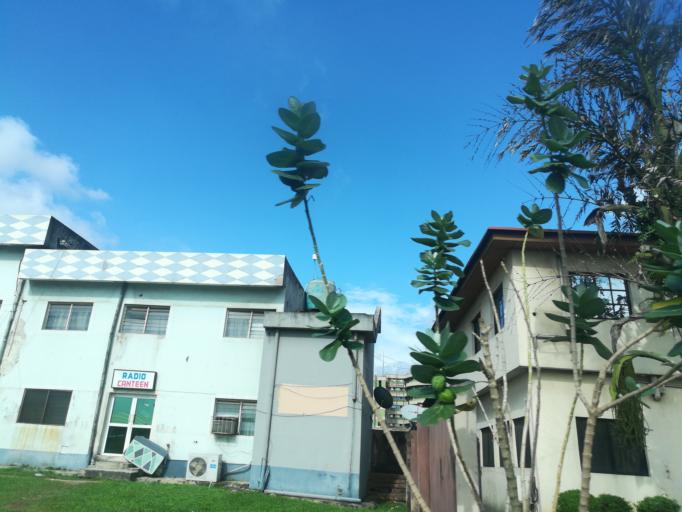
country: NG
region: Lagos
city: Ikeja
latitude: 6.6169
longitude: 3.3550
